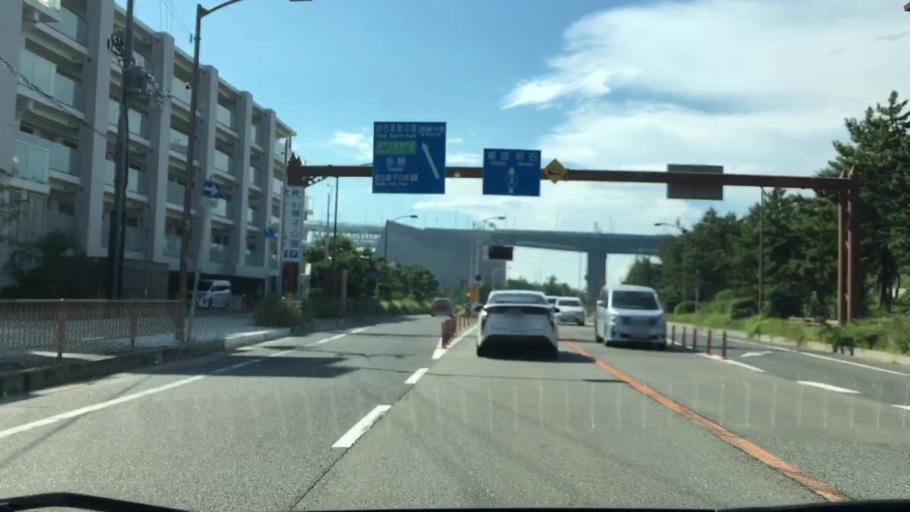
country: JP
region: Hyogo
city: Akashi
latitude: 34.6294
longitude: 135.0392
